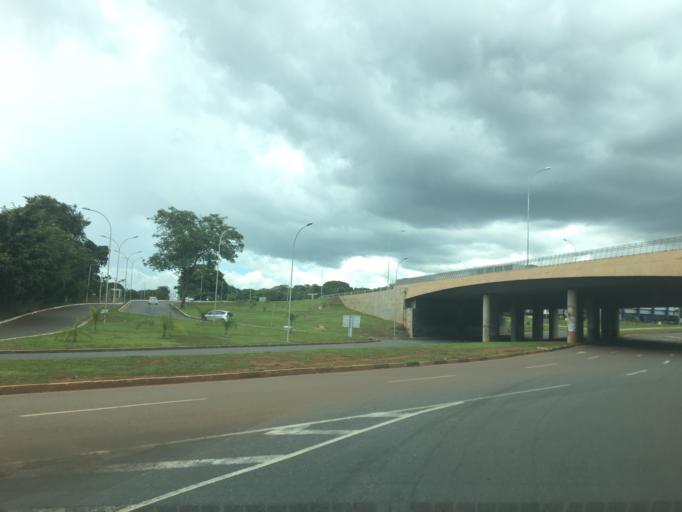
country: BR
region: Federal District
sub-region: Brasilia
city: Brasilia
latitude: -15.8307
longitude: -47.9298
